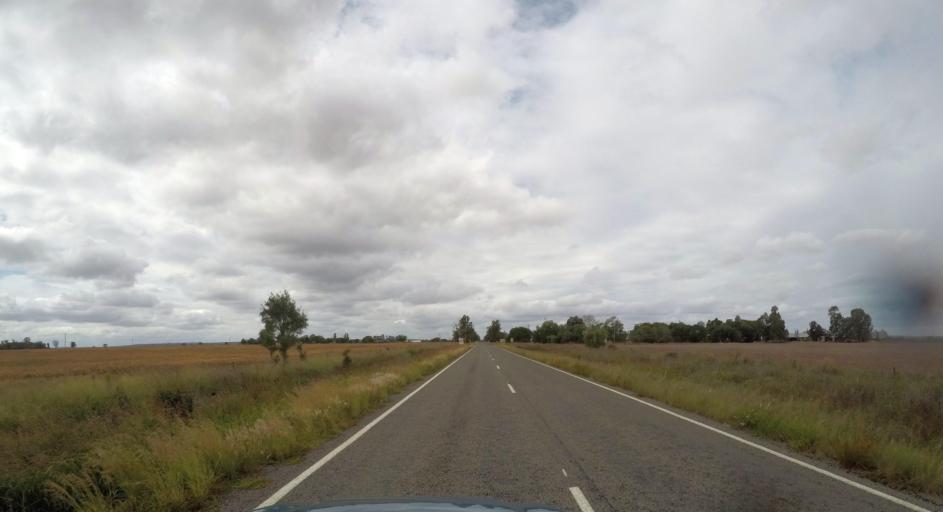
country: AU
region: Queensland
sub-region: South Burnett
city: Kingaroy
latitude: -26.3943
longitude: 151.2368
